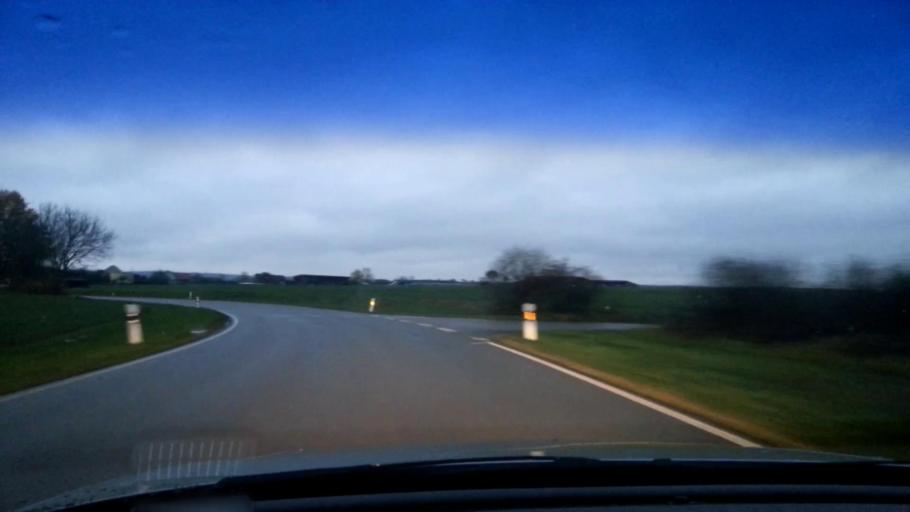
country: DE
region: Bavaria
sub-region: Upper Franconia
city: Schesslitz
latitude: 49.9557
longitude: 11.0248
